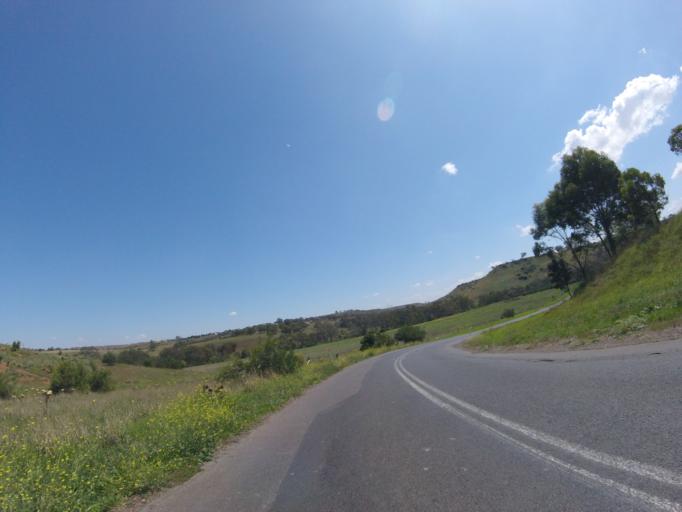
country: AU
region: Victoria
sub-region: Hume
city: Greenvale
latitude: -37.6139
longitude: 144.8049
